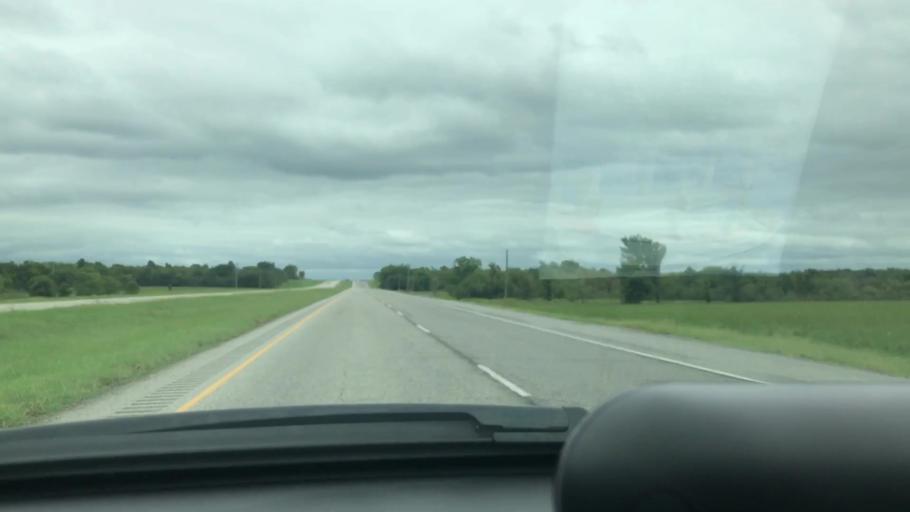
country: US
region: Oklahoma
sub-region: Wagoner County
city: Wagoner
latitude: 35.9848
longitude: -95.3769
